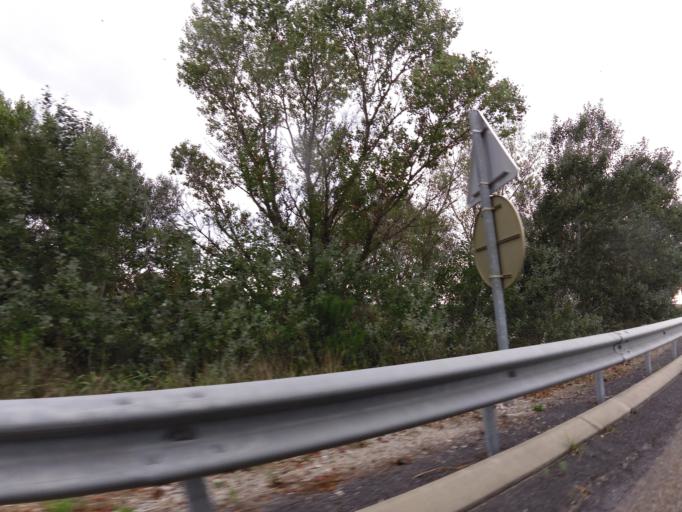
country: FR
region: Languedoc-Roussillon
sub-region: Departement du Gard
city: Aigues-Mortes
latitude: 43.5801
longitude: 4.2000
